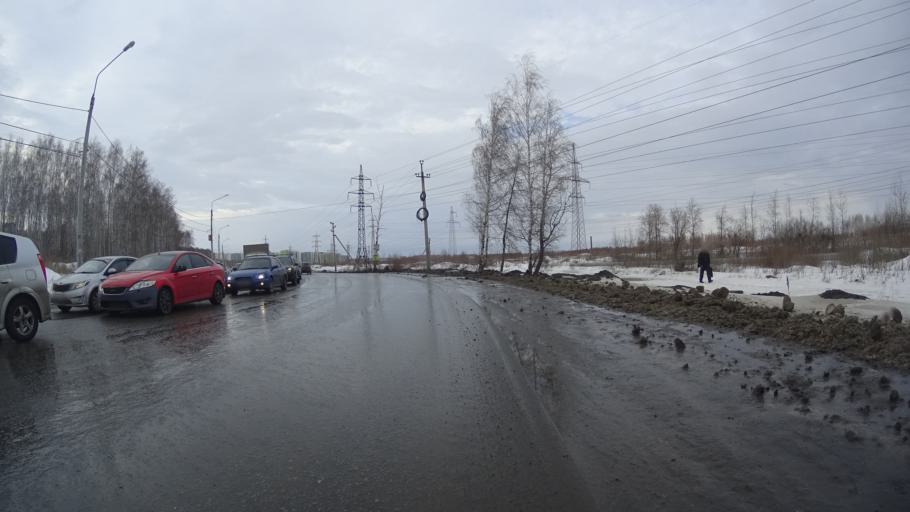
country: RU
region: Chelyabinsk
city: Roshchino
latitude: 55.2090
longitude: 61.3171
